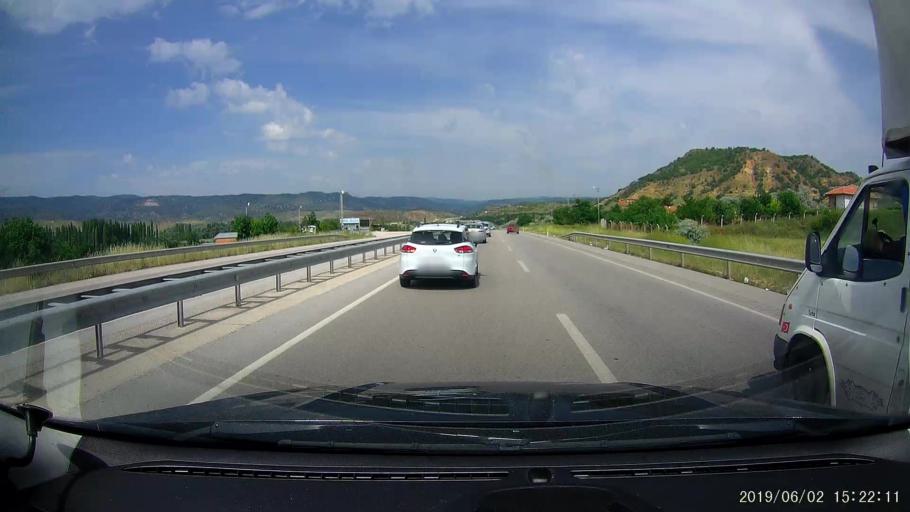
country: TR
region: Corum
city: Osmancik
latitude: 40.9816
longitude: 34.9511
